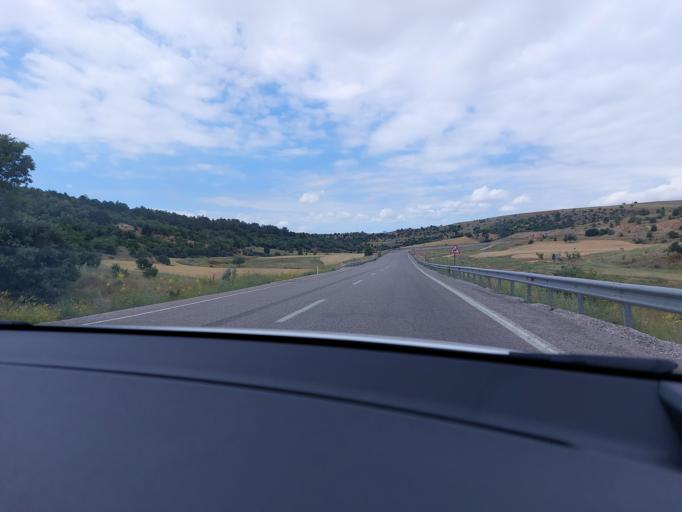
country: TR
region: Konya
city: Doganbey
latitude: 37.8963
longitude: 31.8037
